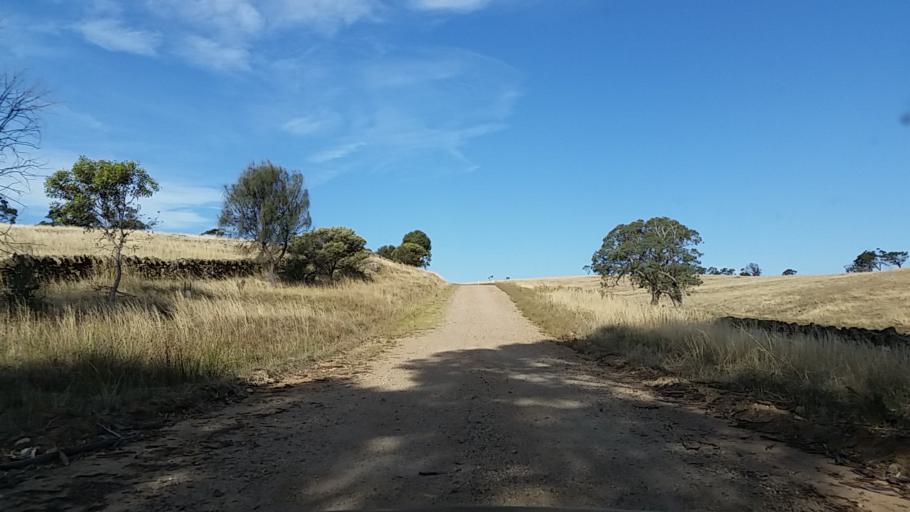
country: AU
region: South Australia
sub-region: Barossa
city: Angaston
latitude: -34.6130
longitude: 139.1740
